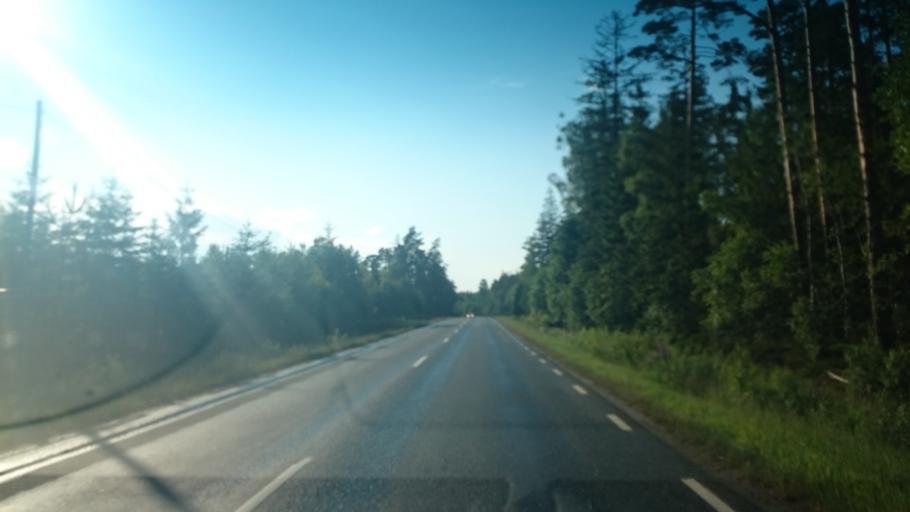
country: SE
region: Skane
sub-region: Osby Kommun
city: Lonsboda
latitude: 56.4280
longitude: 14.2715
